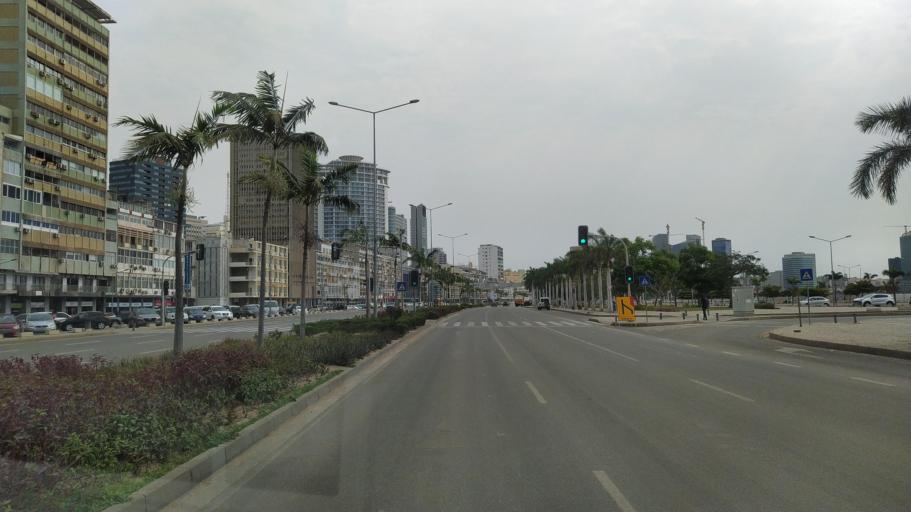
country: AO
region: Luanda
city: Luanda
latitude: -8.8041
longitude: 13.2409
